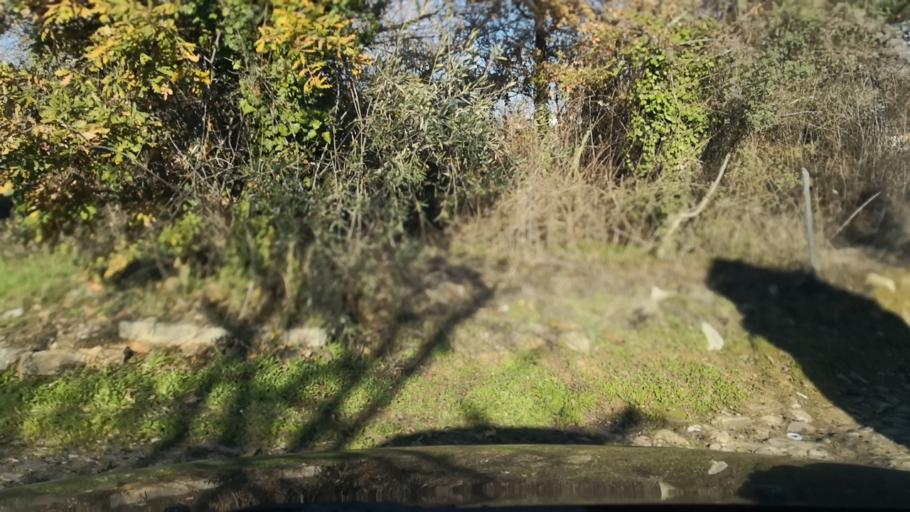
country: PT
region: Vila Real
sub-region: Vila Real
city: Vila Real
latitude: 41.2883
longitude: -7.7258
